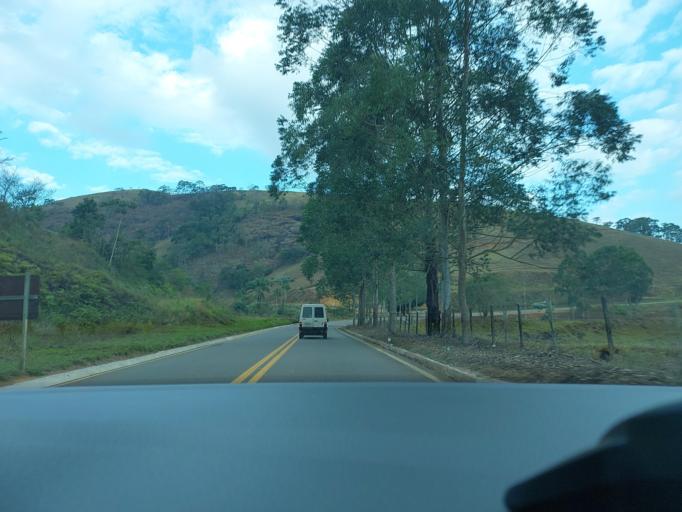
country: BR
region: Minas Gerais
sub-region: Mirai
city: Mirai
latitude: -21.0316
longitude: -42.5365
